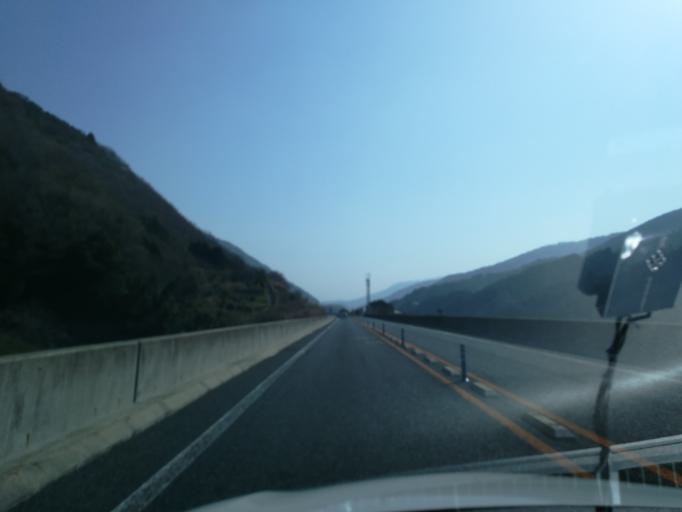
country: JP
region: Tokushima
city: Ikedacho
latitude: 34.0073
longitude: 133.7186
